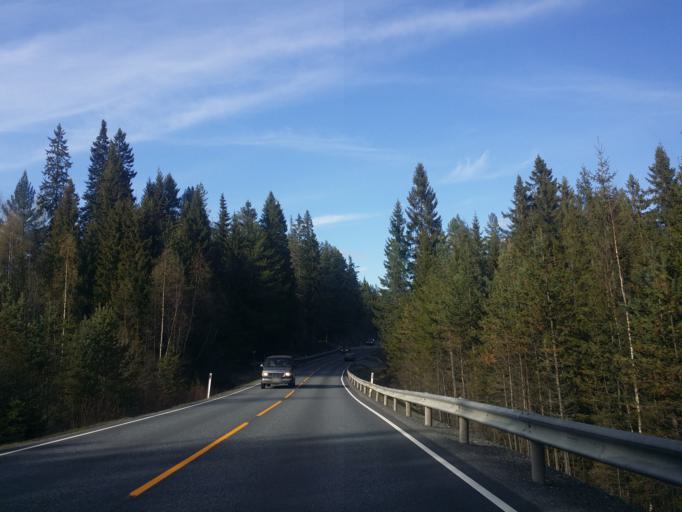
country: NO
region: Buskerud
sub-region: Kongsberg
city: Kongsberg
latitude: 59.6160
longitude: 9.4665
